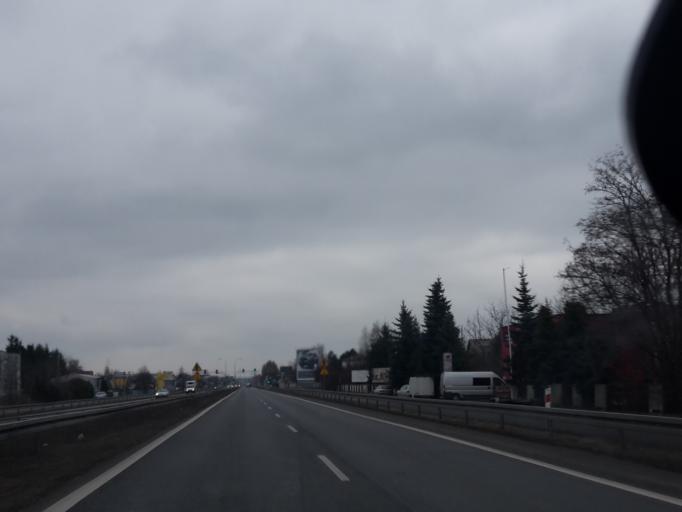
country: PL
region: Masovian Voivodeship
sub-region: Powiat warszawski zachodni
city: Lomianki
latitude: 52.3372
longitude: 20.8768
